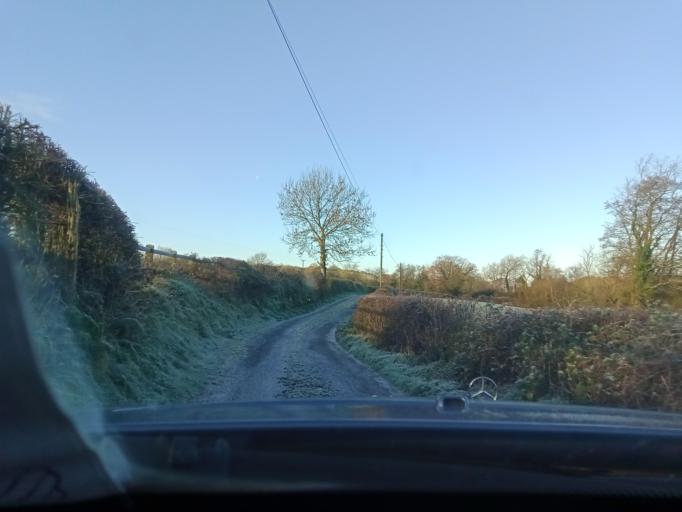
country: IE
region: Leinster
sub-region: Kilkenny
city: Graiguenamanagh
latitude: 52.5980
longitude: -6.9505
